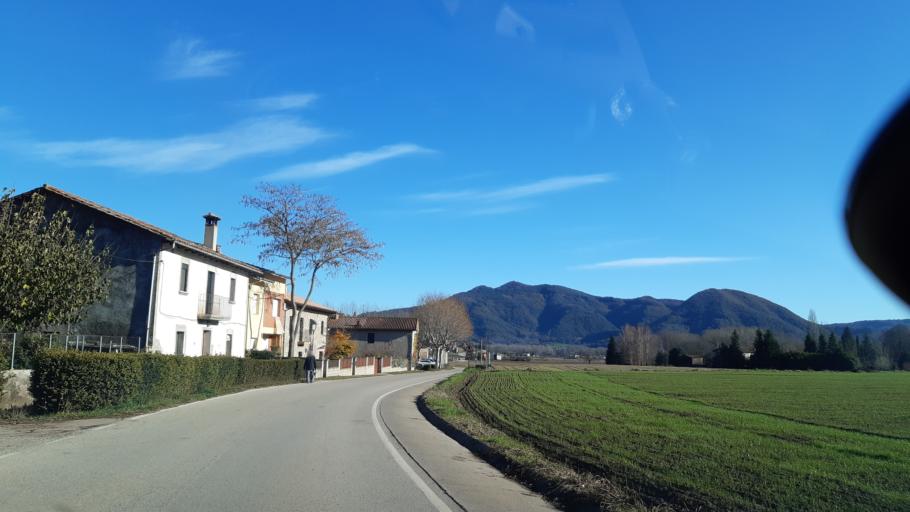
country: ES
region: Catalonia
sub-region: Provincia de Girona
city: Bas
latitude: 42.1503
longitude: 2.4227
